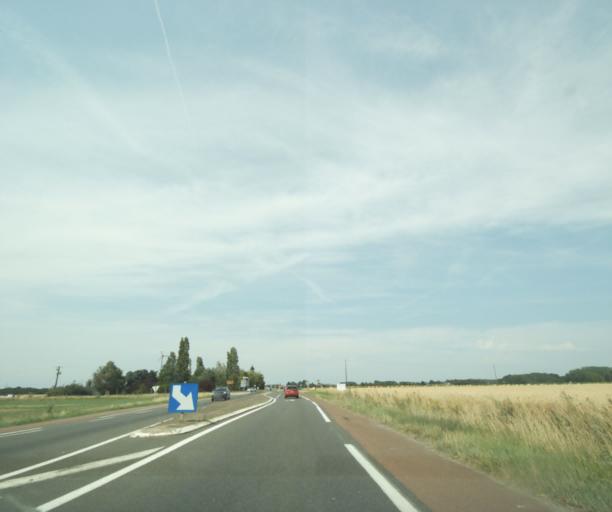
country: FR
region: Centre
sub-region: Departement d'Indre-et-Loire
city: Sorigny
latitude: 47.1981
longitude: 0.6694
